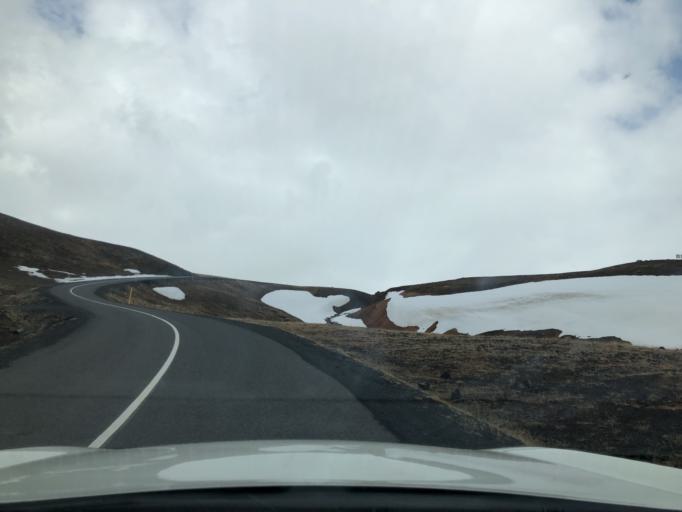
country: IS
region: Northeast
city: Laugar
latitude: 65.7091
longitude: -16.7708
